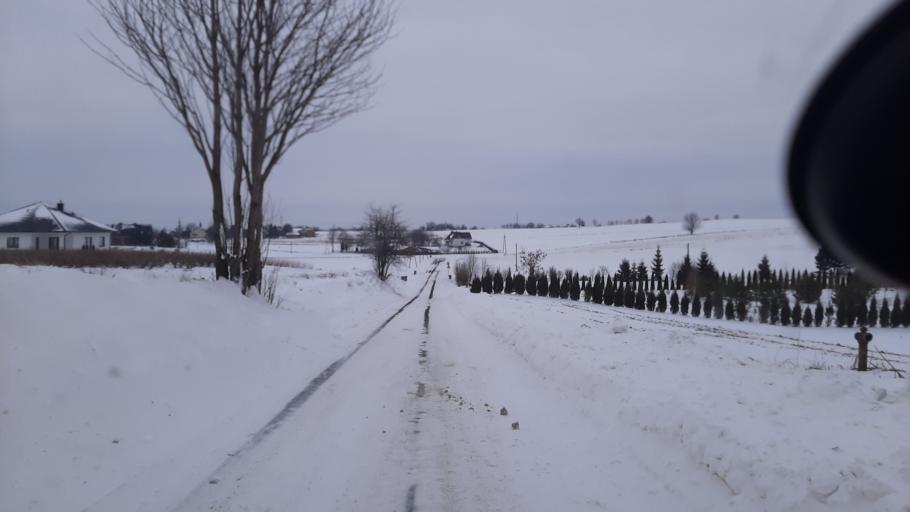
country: PL
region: Lublin Voivodeship
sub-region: Powiat lubelski
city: Garbow
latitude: 51.3375
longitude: 22.2928
